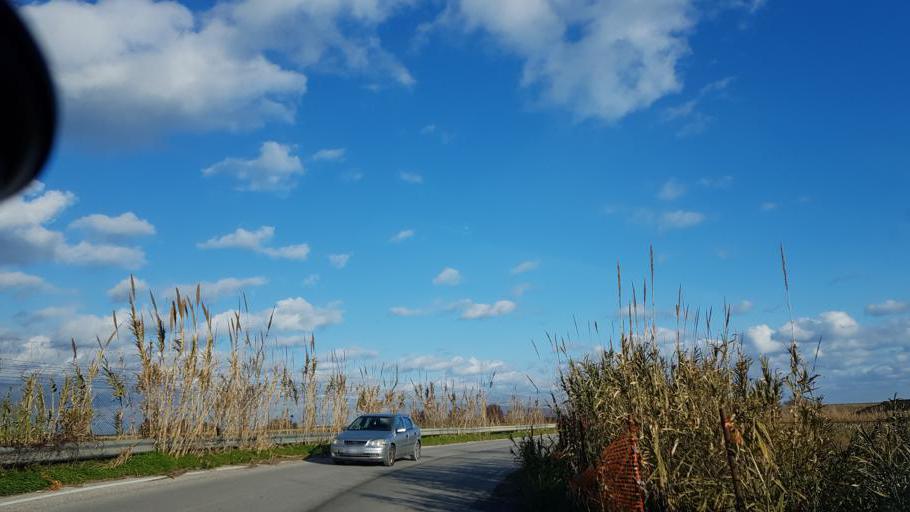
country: IT
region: Apulia
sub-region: Provincia di Brindisi
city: Materdomini
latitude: 40.6609
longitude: 17.9571
